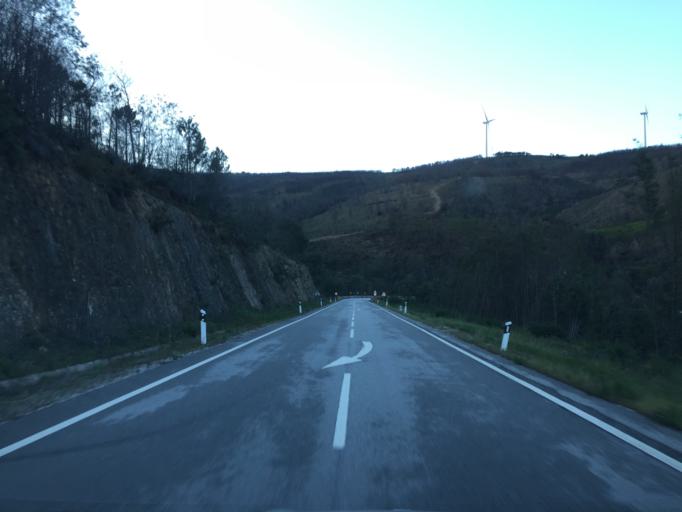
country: PT
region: Coimbra
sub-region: Pampilhosa da Serra
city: Pampilhosa da Serra
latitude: 40.1008
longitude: -7.9896
